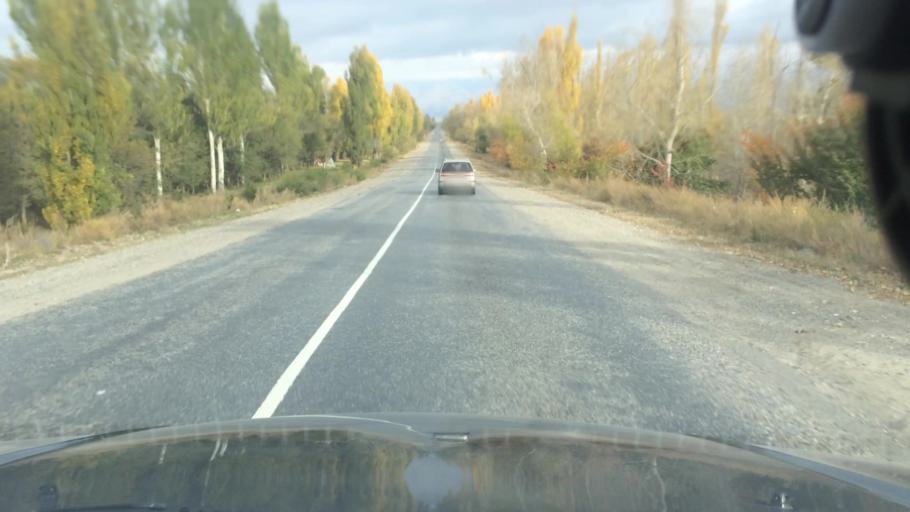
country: KG
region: Ysyk-Koel
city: Tyup
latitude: 42.6111
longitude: 78.3669
